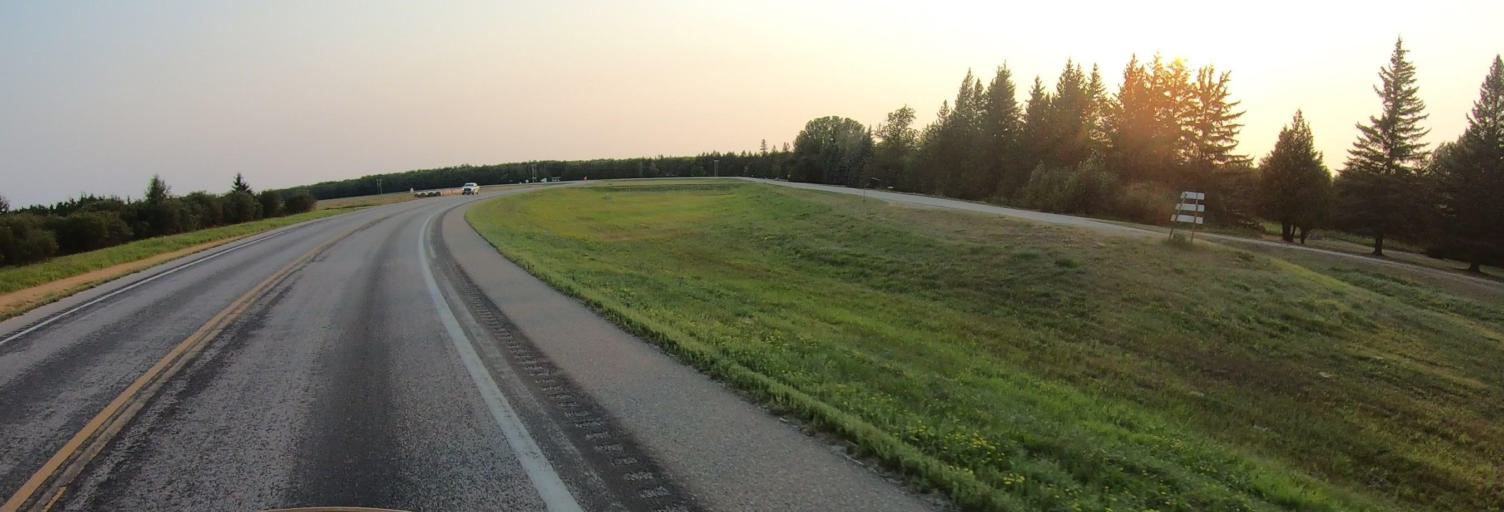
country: US
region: Minnesota
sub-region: Roseau County
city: Warroad
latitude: 48.8706
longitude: -95.3236
